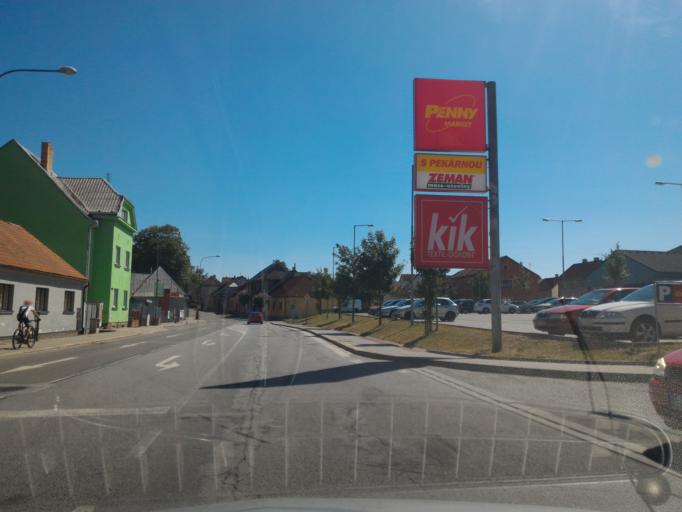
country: CZ
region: Vysocina
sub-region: Okres Jihlava
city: Trest'
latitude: 49.2869
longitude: 15.4812
